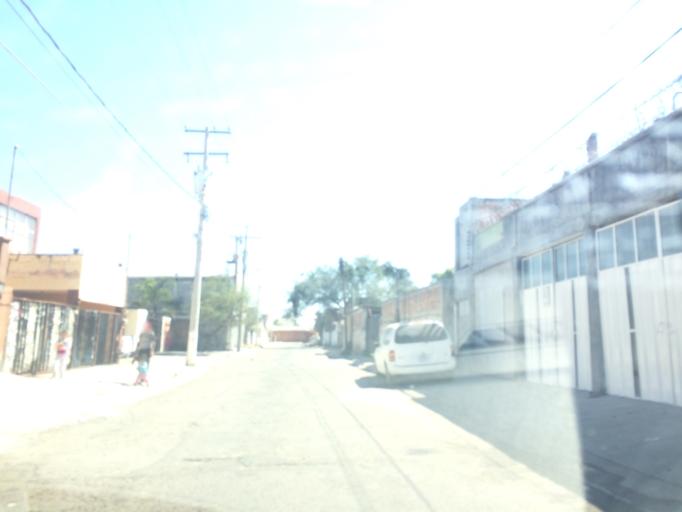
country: MX
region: Guanajuato
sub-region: Leon
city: San Jose de Duran (Los Troncoso)
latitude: 21.0888
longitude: -101.6625
